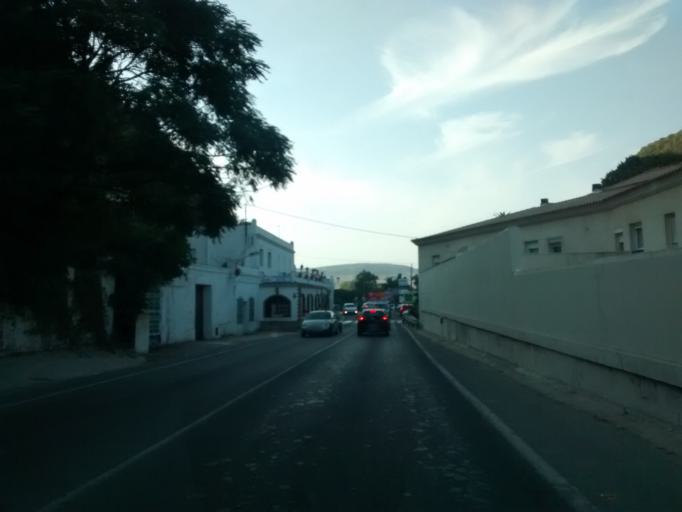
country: ES
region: Andalusia
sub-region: Provincia de Cadiz
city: Vejer de la Frontera
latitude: 36.2528
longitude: -5.9563
